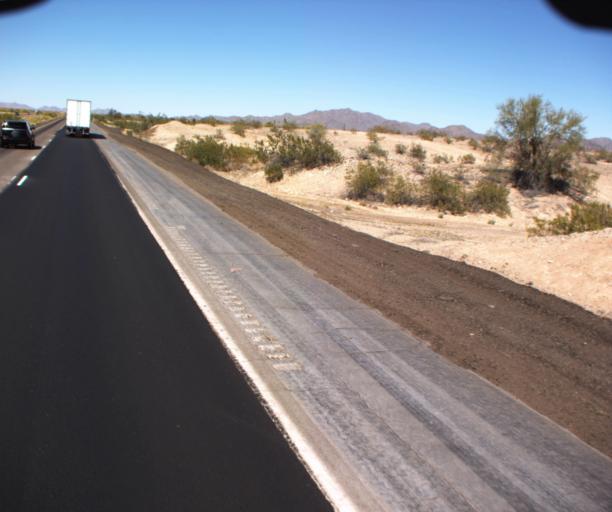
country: US
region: Arizona
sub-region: Maricopa County
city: Gila Bend
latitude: 33.0627
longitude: -112.6448
